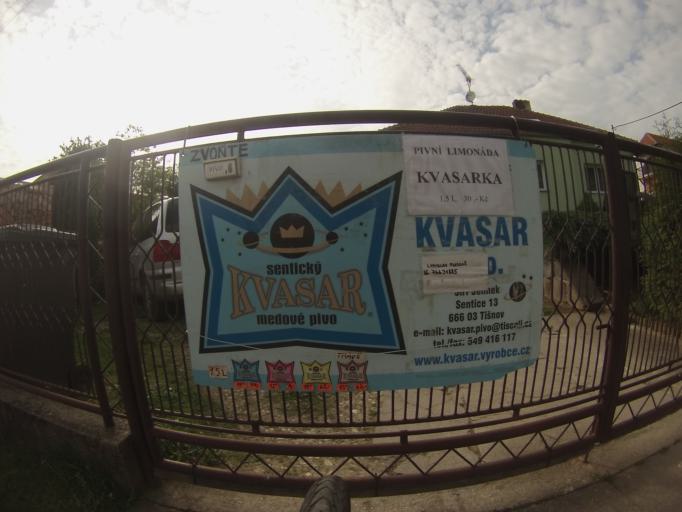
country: CZ
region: South Moravian
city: Cebin
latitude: 49.3144
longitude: 16.4533
